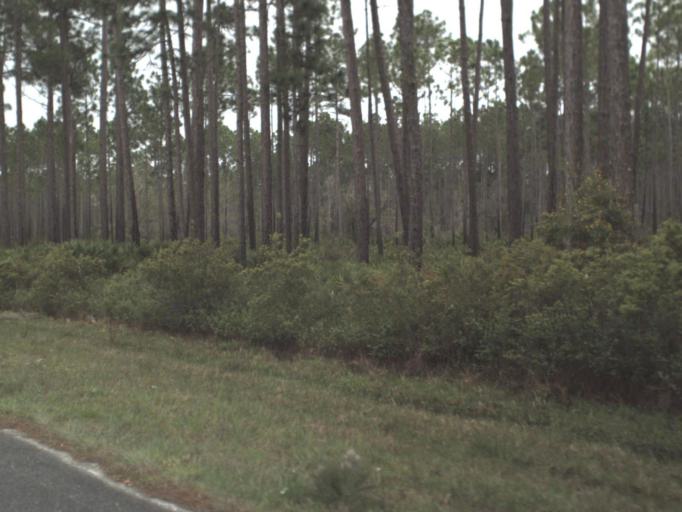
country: US
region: Florida
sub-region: Franklin County
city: Eastpoint
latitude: 29.8158
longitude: -84.8465
